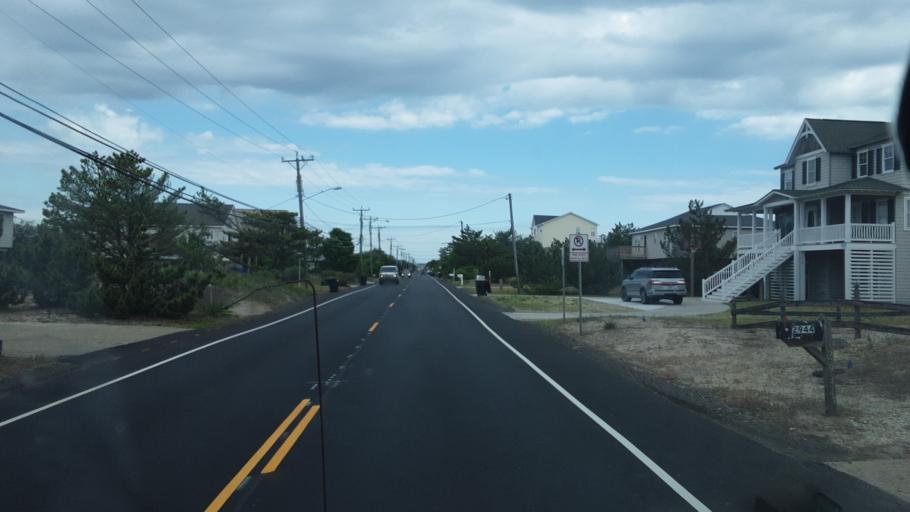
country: US
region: Virginia
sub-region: City of Virginia Beach
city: Virginia Beach
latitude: 36.7260
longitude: -75.9376
